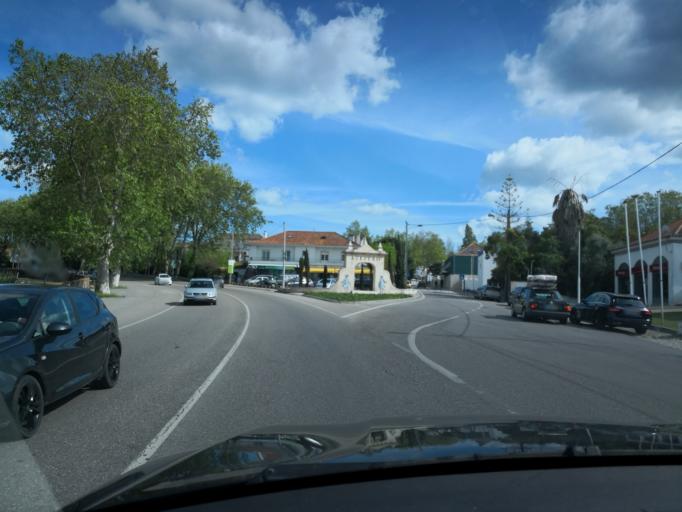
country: PT
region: Setubal
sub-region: Palmela
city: Quinta do Anjo
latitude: 38.5203
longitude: -9.0149
